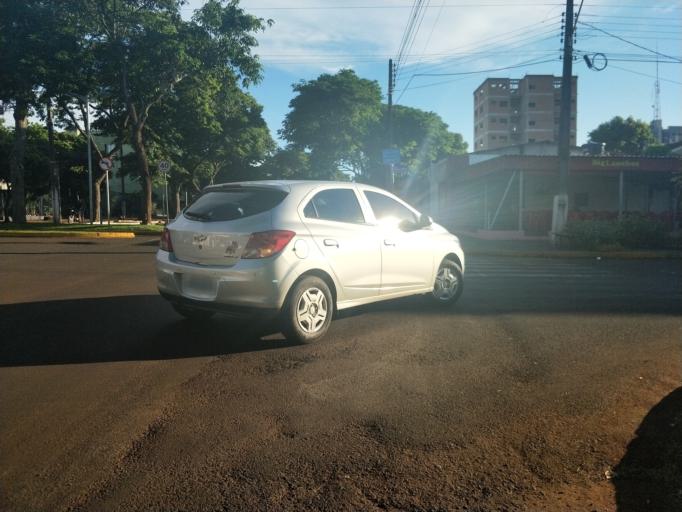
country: BR
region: Parana
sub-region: Marechal Candido Rondon
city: Marechal Candido Rondon
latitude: -24.5598
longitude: -54.0578
